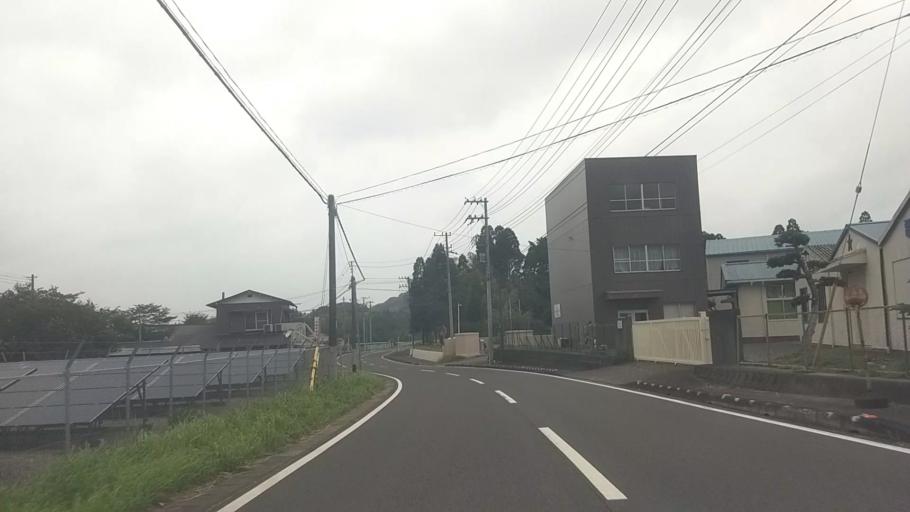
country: JP
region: Chiba
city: Ohara
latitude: 35.2653
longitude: 140.2547
